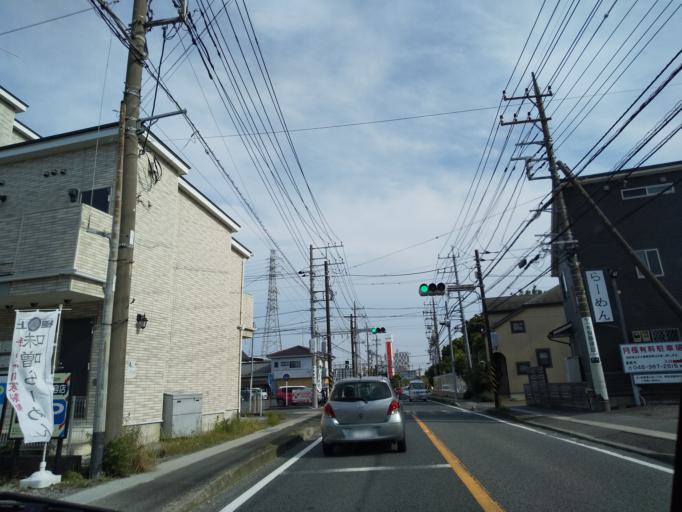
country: JP
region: Kanagawa
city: Zama
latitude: 35.4926
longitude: 139.3397
